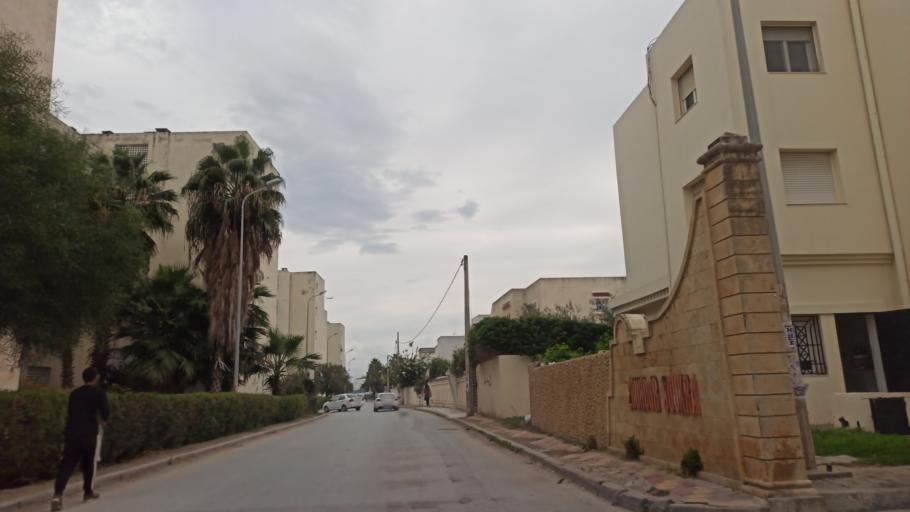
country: TN
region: Tunis
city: La Goulette
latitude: 36.8564
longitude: 10.2675
